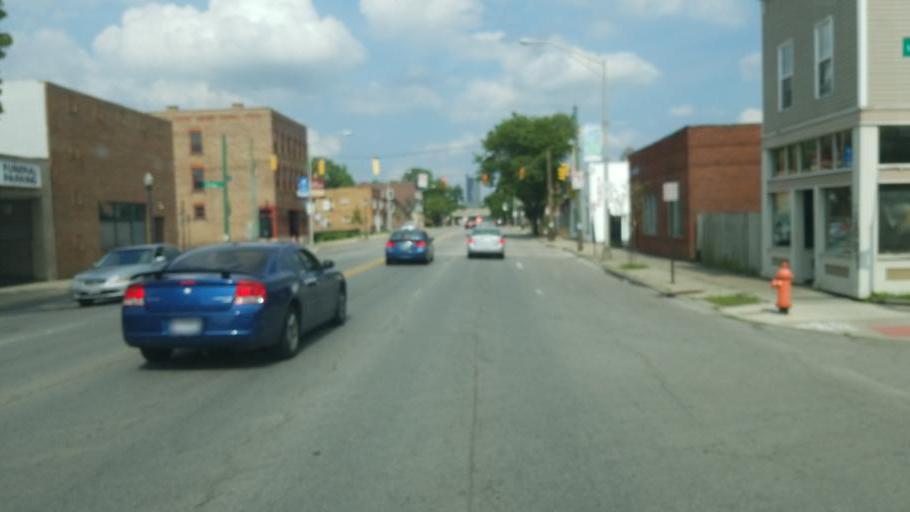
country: US
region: Ohio
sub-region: Franklin County
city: Grandview Heights
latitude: 39.9580
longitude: -83.0347
